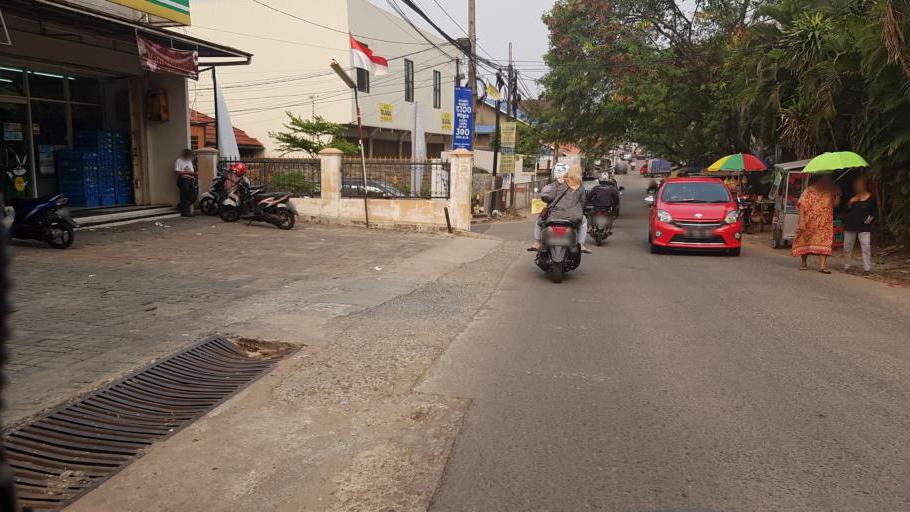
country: ID
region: West Java
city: Depok
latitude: -6.3723
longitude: 106.8533
